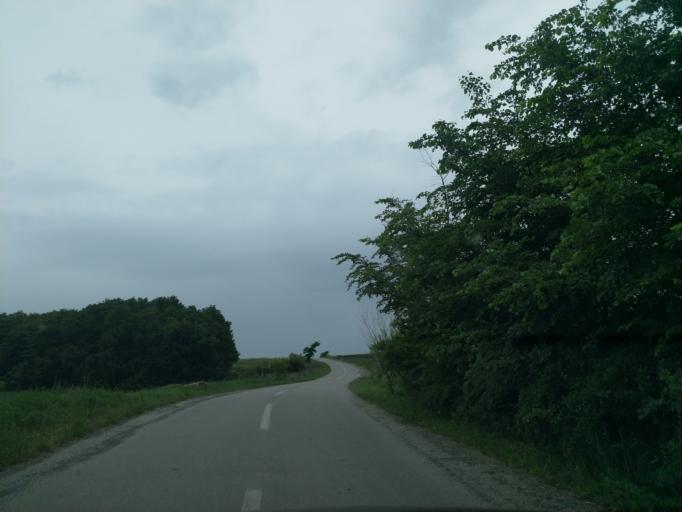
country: RS
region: Central Serbia
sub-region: Pomoravski Okrug
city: Paracin
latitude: 43.8729
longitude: 21.5695
